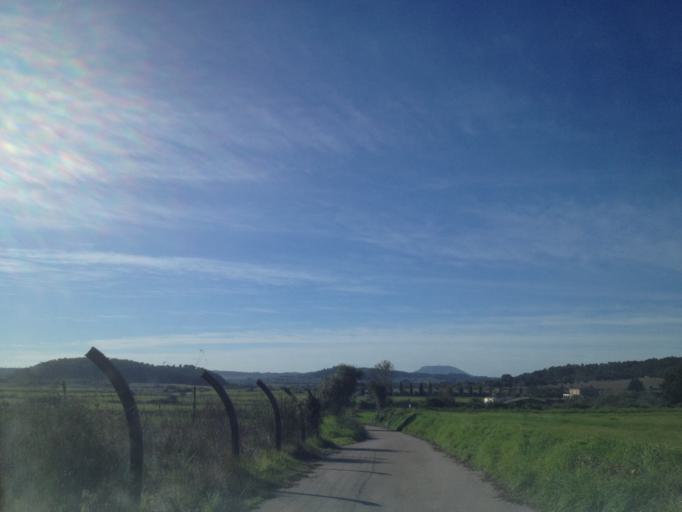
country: ES
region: Balearic Islands
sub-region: Illes Balears
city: Sineu
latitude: 39.6520
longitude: 3.0384
